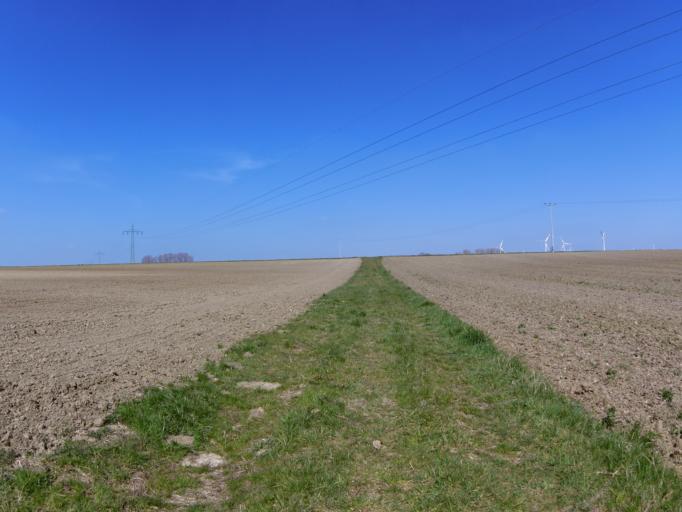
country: DE
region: Bavaria
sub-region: Regierungsbezirk Unterfranken
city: Biebelried
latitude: 49.7349
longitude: 10.0904
